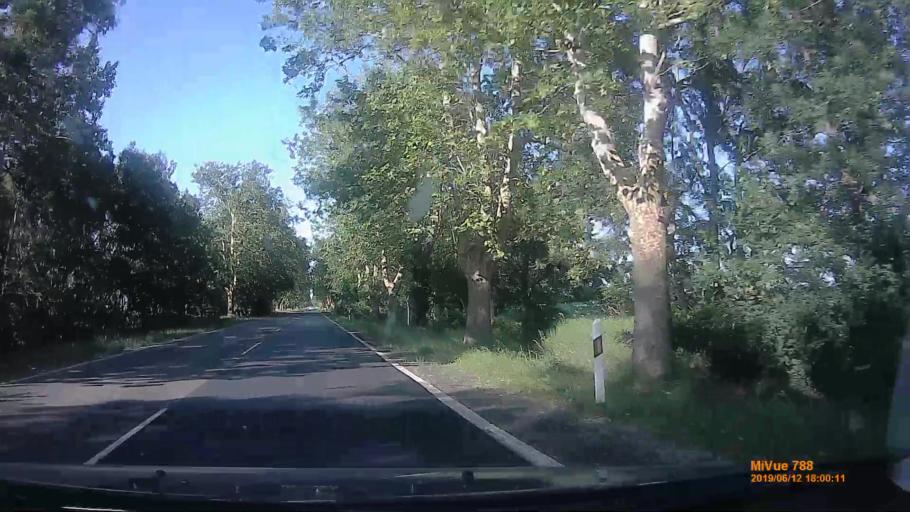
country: HU
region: Csongrad
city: Roszke
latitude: 46.2143
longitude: 20.0580
